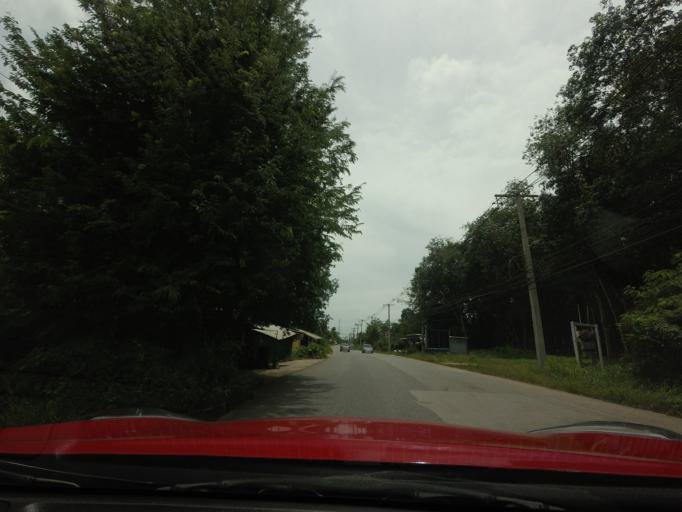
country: TH
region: Songkhla
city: Hat Yai
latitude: 7.0019
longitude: 100.5270
